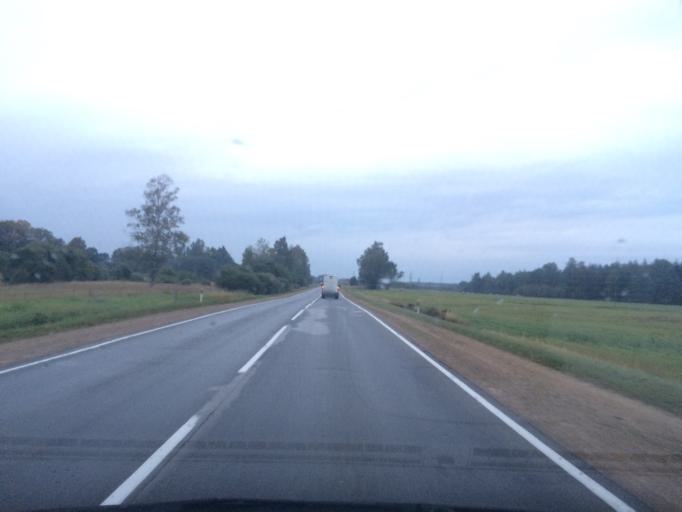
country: LV
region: Plavinu
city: Plavinas
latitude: 56.5945
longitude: 25.7805
